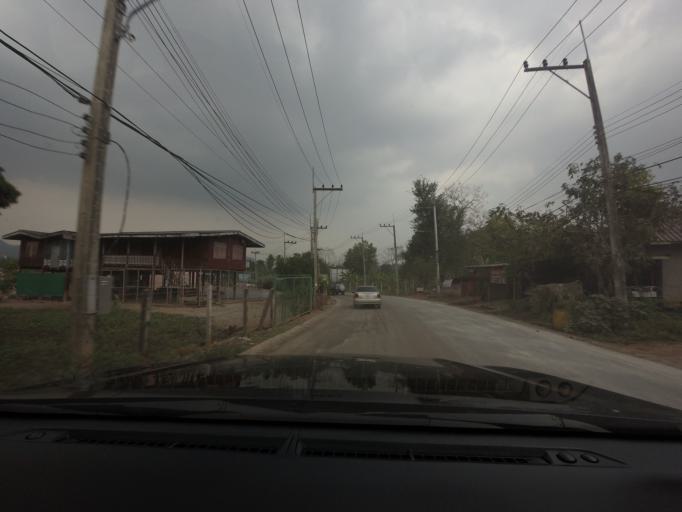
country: TH
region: Nakhon Ratchasima
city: Pak Chong
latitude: 14.5135
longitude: 101.4443
